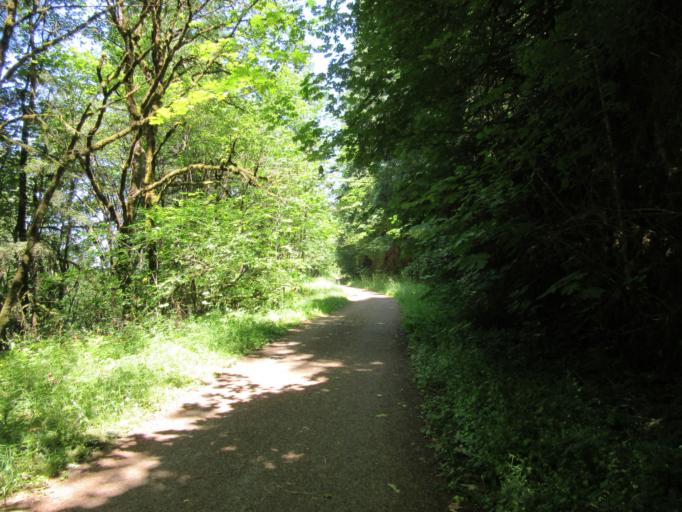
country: US
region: Oregon
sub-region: Washington County
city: West Haven
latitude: 45.5544
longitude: -122.7519
